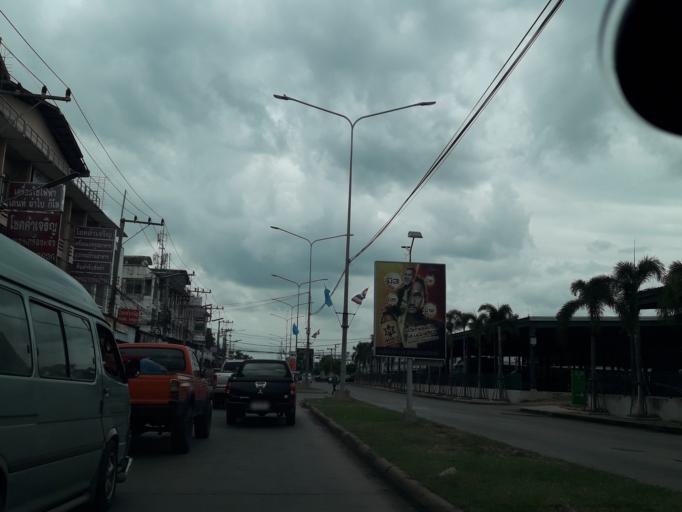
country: TH
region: Pathum Thani
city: Khlong Luang
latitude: 14.0818
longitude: 100.6326
